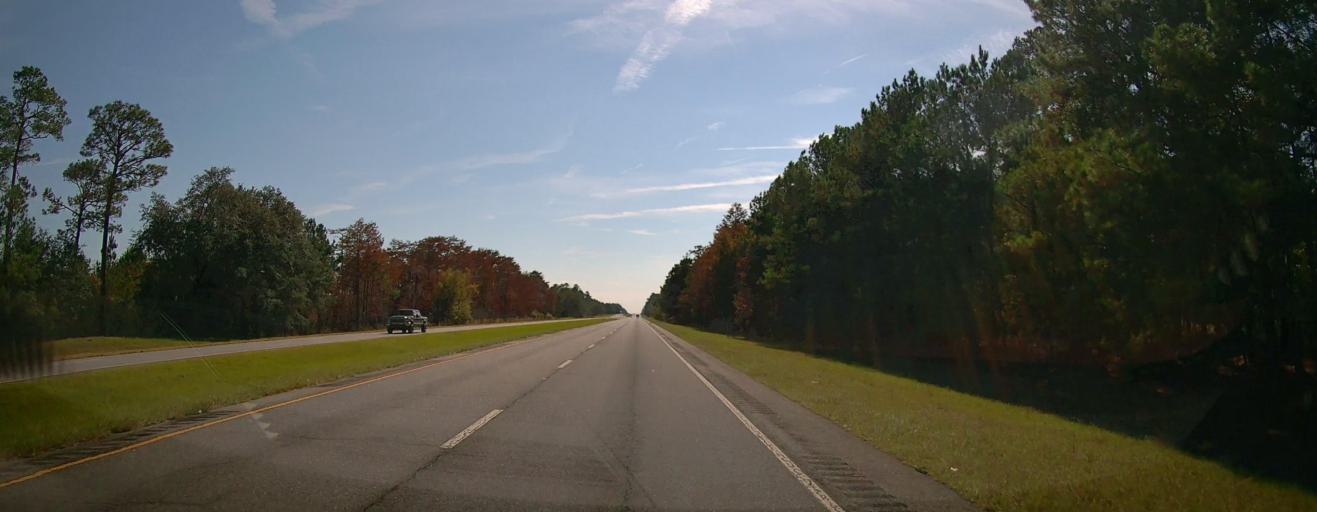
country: US
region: Georgia
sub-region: Lee County
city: Leesburg
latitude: 31.7040
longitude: -83.9909
